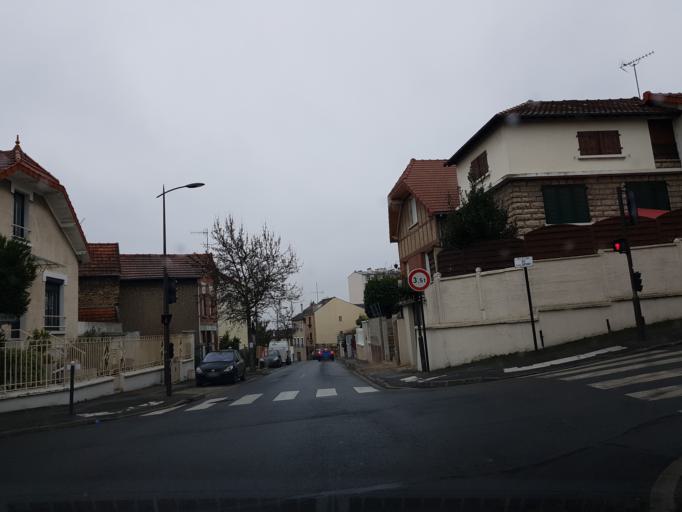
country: FR
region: Ile-de-France
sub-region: Departement du Val-de-Marne
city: Thiais
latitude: 48.7686
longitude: 2.3925
